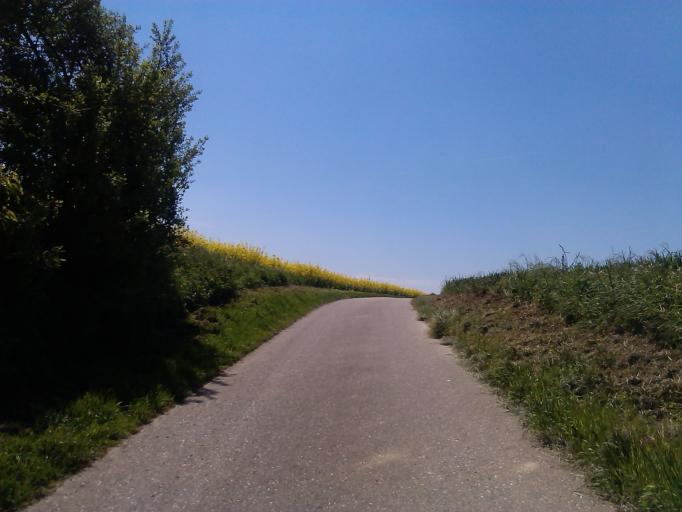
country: DE
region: Baden-Wuerttemberg
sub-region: Karlsruhe Region
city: Sulzfeld
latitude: 49.1214
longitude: 8.8824
